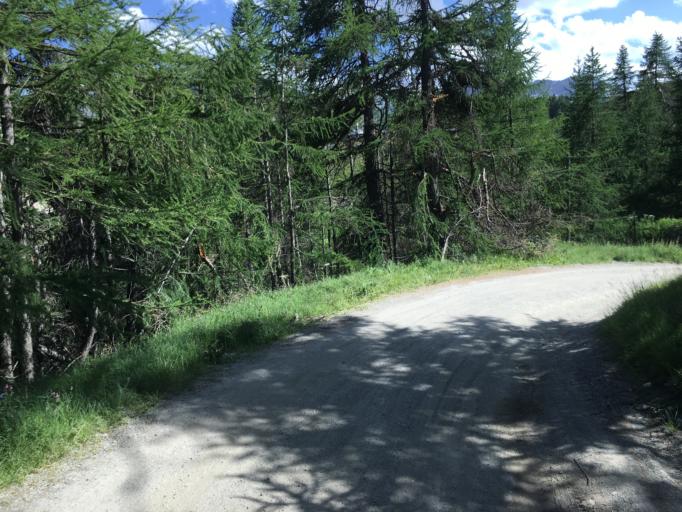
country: IT
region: Piedmont
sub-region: Provincia di Torino
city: Sestriere
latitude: 44.9660
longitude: 6.8815
